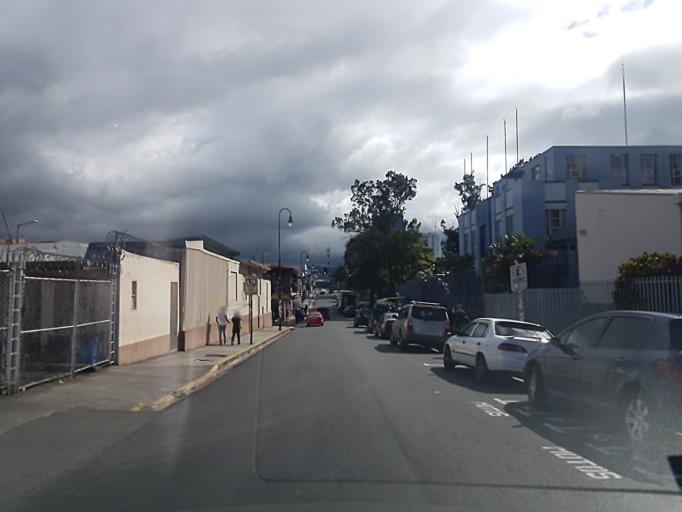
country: CR
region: San Jose
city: San Jose
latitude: 9.9328
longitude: -84.0851
